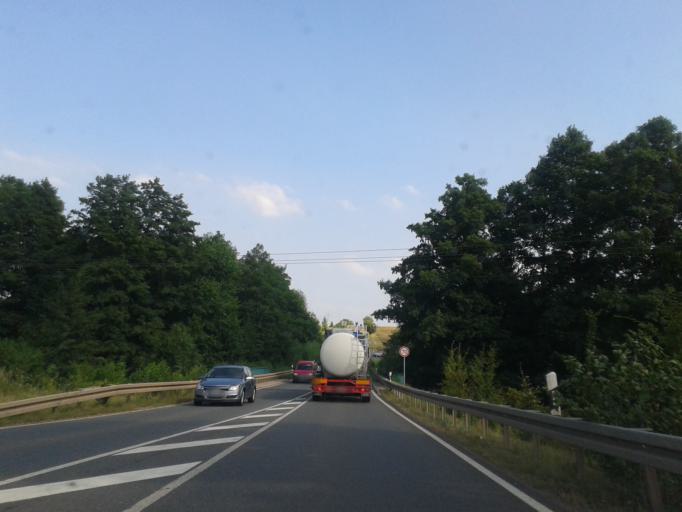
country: DE
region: Saxony
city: Wilsdruff
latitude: 51.0508
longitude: 13.5483
